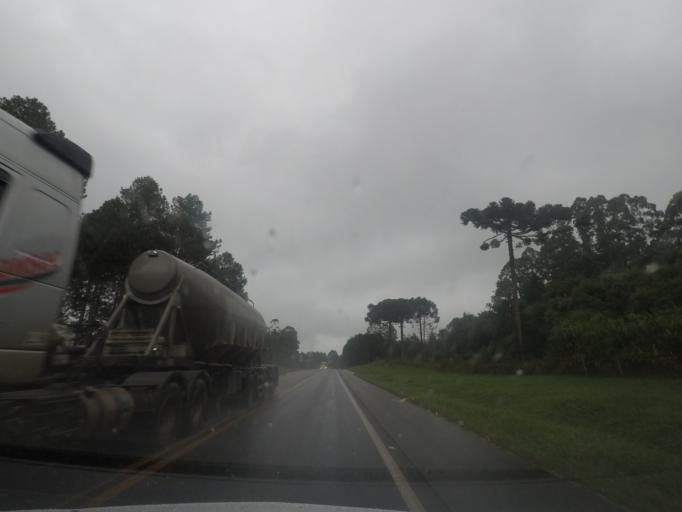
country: BR
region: Parana
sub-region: Colombo
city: Colombo
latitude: -25.3297
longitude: -49.1594
